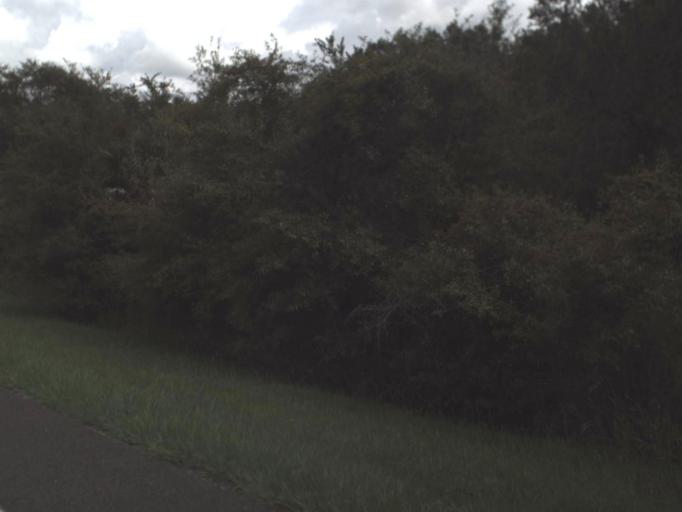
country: US
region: Florida
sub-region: Sarasota County
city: North Port
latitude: 27.1934
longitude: -82.1492
